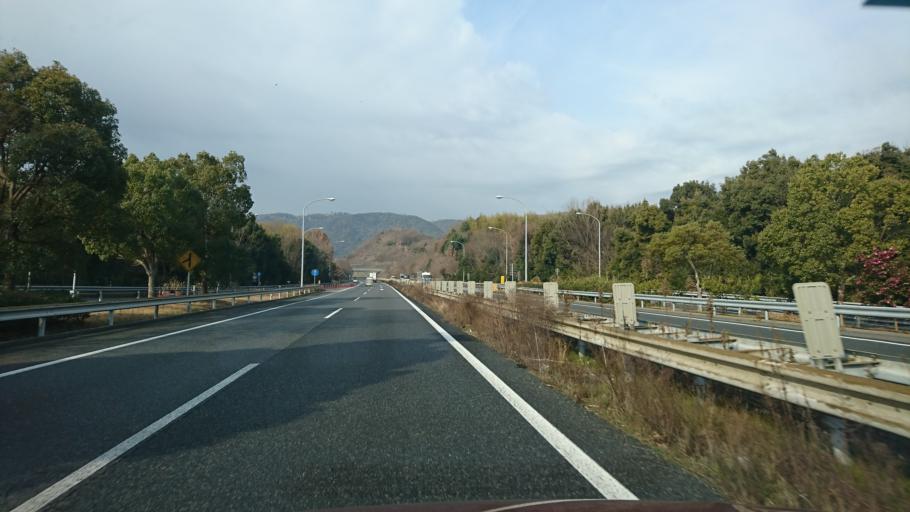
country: JP
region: Okayama
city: Kamogatacho-kamogata
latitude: 34.5674
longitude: 133.6433
